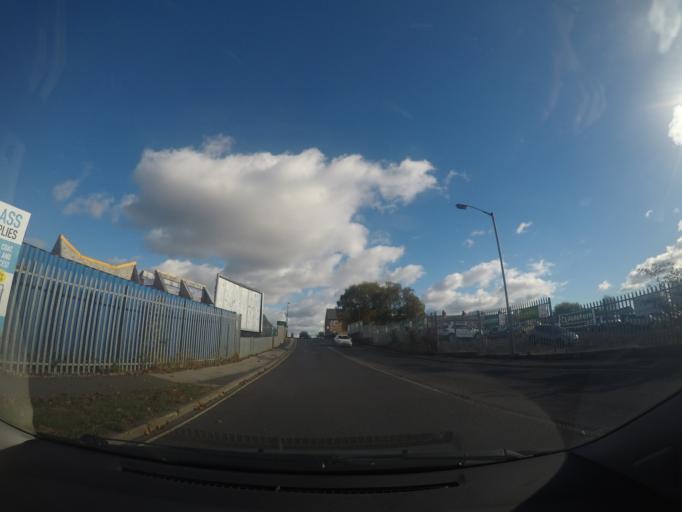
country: GB
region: England
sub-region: City of York
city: York
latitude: 53.9617
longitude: -1.1049
